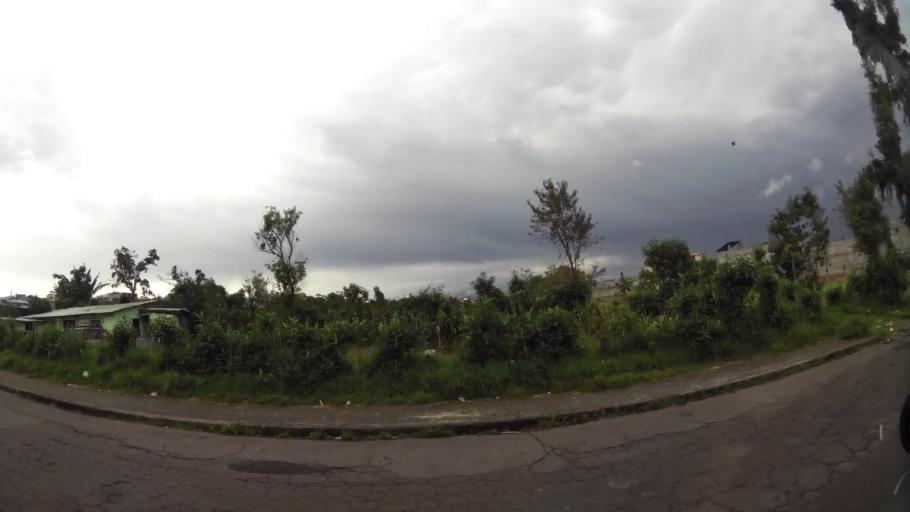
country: EC
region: Pichincha
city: Sangolqui
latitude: -0.3528
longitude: -78.5554
